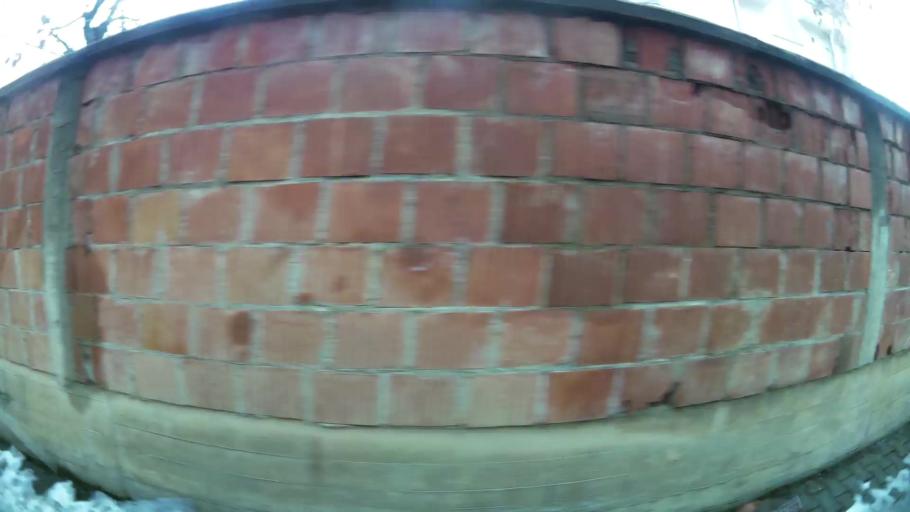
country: XK
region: Pristina
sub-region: Komuna e Prishtines
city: Pristina
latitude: 42.6801
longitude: 21.1743
